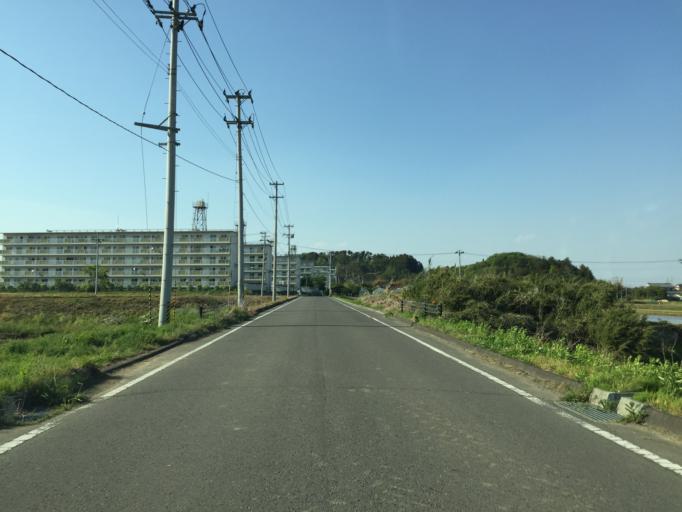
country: JP
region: Fukushima
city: Koriyama
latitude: 37.4031
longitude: 140.3214
